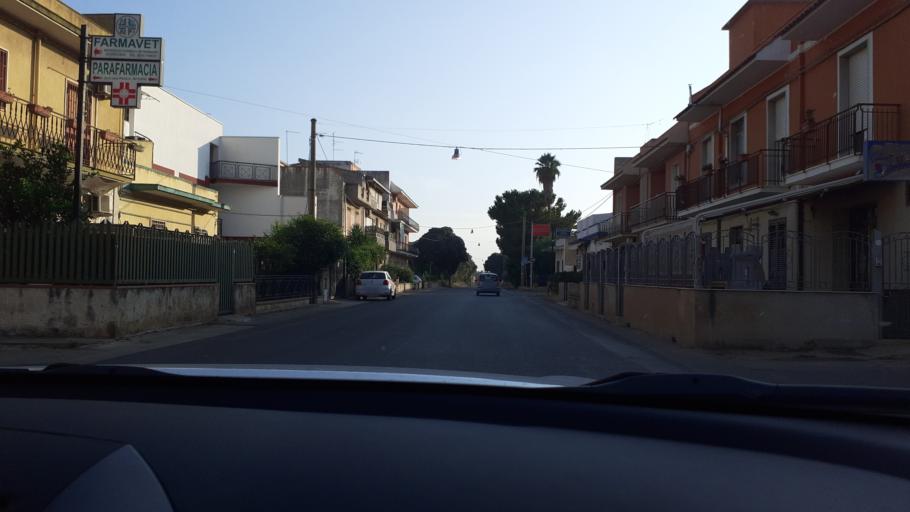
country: IT
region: Sicily
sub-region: Provincia di Siracusa
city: Cassibile
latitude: 36.9753
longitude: 15.1958
